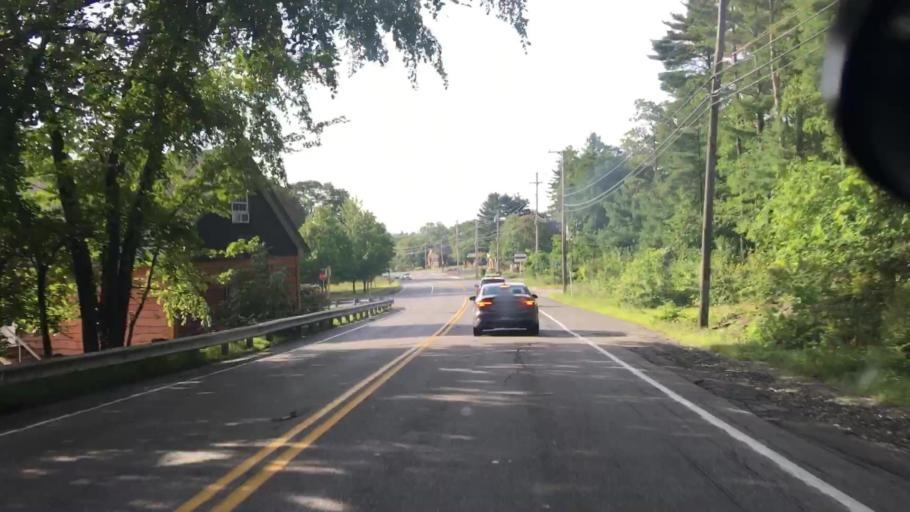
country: US
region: Maine
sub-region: Cumberland County
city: Westbrook
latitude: 43.7157
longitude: -70.3355
